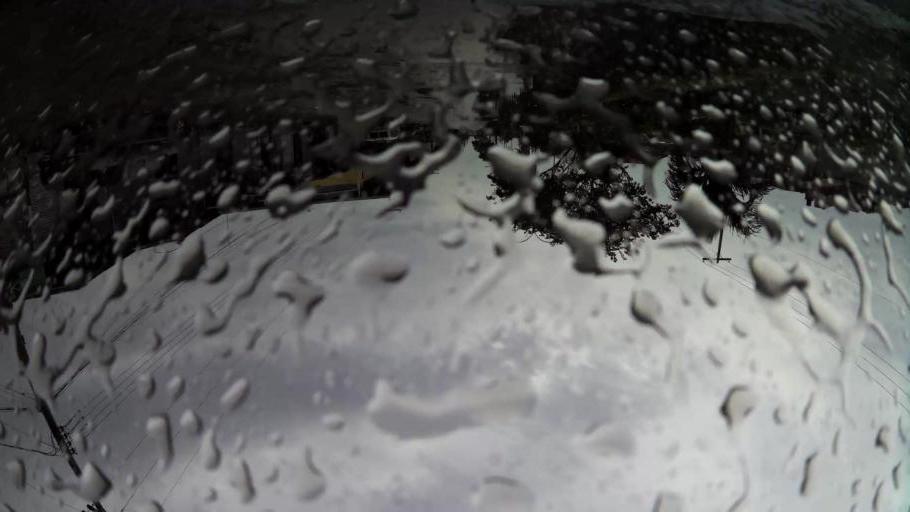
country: BO
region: Santa Cruz
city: Santa Cruz de la Sierra
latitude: -17.7903
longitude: -63.1514
